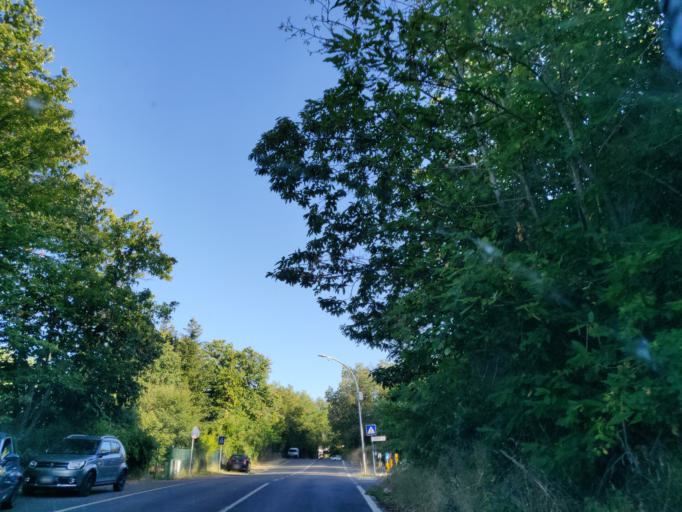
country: IT
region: Tuscany
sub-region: Provincia di Siena
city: Piancastagnaio
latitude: 42.8547
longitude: 11.6844
